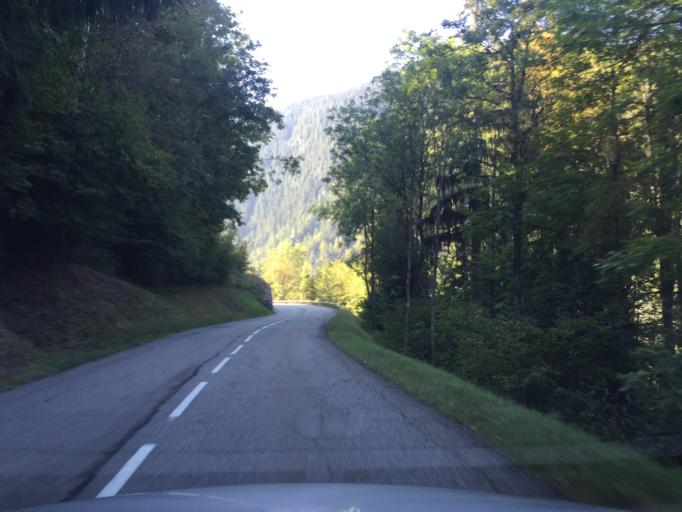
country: FR
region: Rhone-Alpes
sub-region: Departement de la Savoie
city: Belle-Plagne
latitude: 45.5544
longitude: 6.7495
